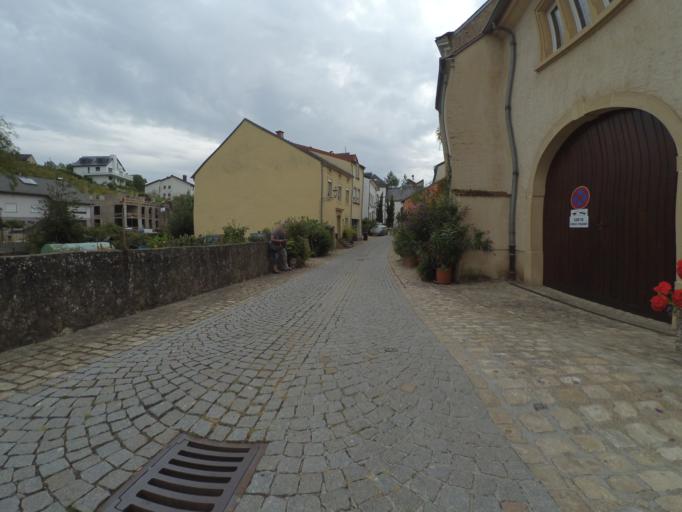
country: LU
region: Grevenmacher
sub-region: Canton de Remich
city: Lenningen
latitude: 49.6024
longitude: 6.3869
